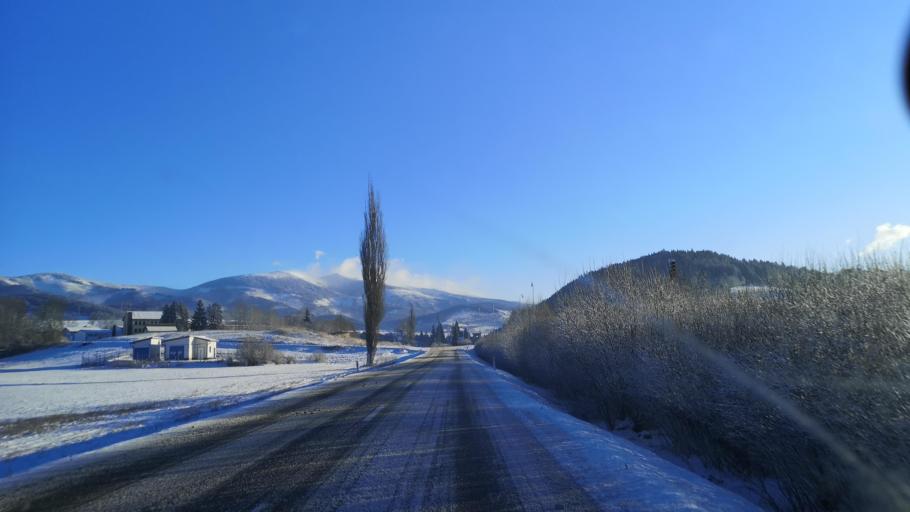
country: SK
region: Banskobystricky
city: Tisovec
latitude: 48.8554
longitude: 19.9502
